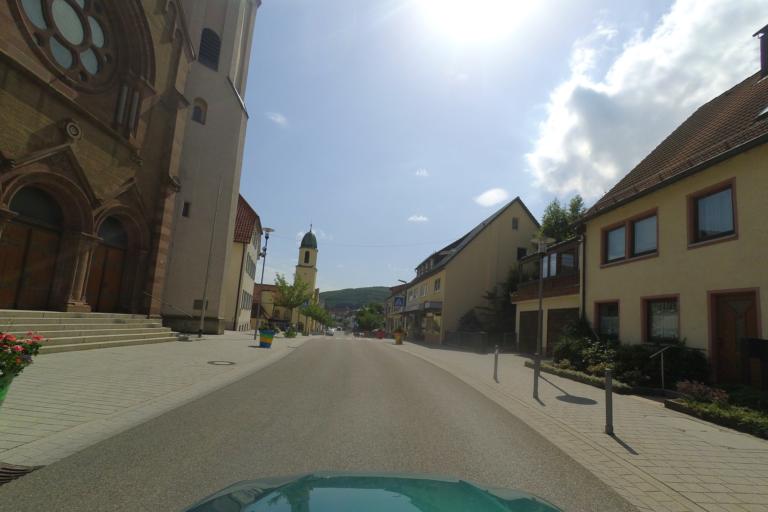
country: DE
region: Baden-Wuerttemberg
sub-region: Regierungsbezirk Stuttgart
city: Oberkochen
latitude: 48.7846
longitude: 10.1065
